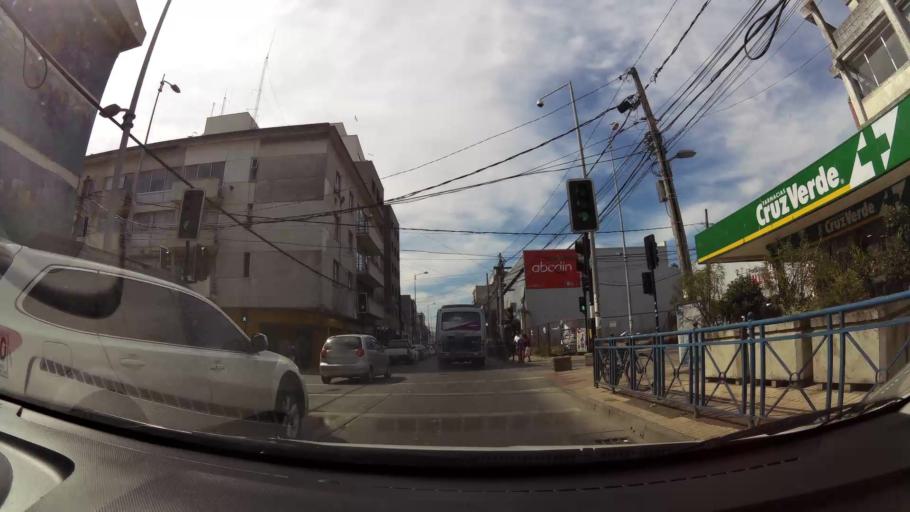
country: CL
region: Biobio
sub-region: Provincia de Concepcion
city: Talcahuano
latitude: -36.7137
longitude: -73.1130
